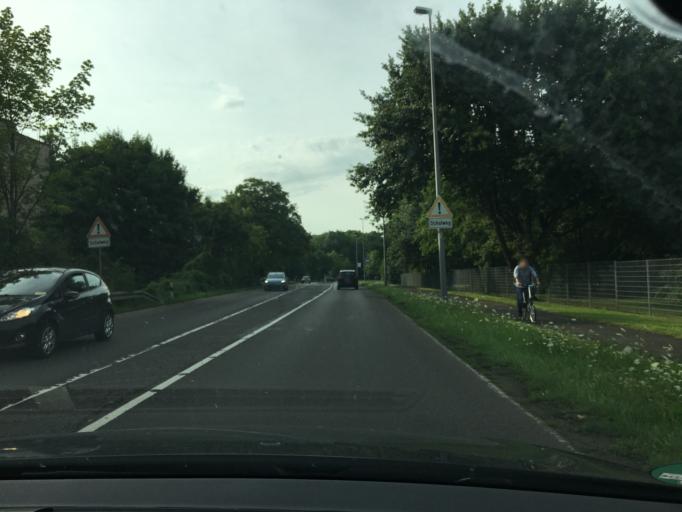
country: DE
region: North Rhine-Westphalia
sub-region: Regierungsbezirk Koln
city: Poll
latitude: 50.8748
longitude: 6.9970
